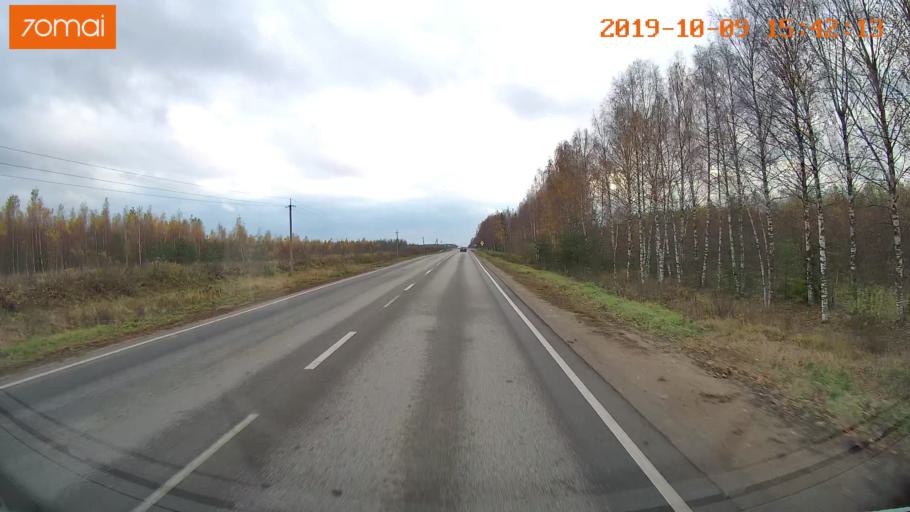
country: RU
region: Kostroma
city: Oktyabr'skiy
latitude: 57.8708
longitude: 41.1107
